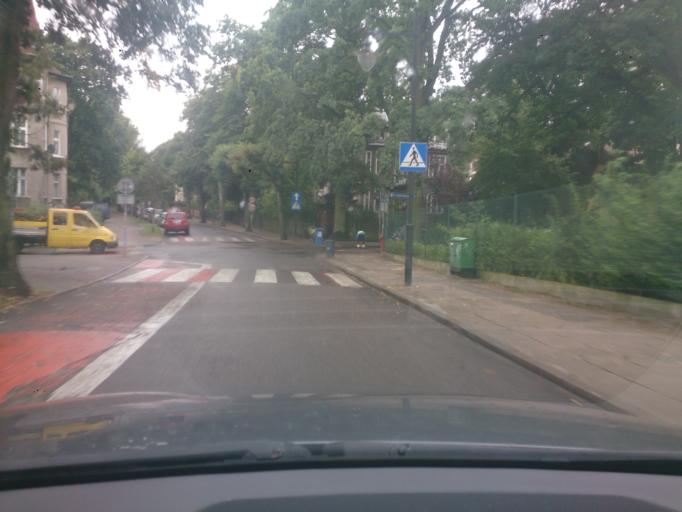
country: PL
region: Pomeranian Voivodeship
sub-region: Sopot
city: Sopot
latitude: 54.4379
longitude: 18.5573
